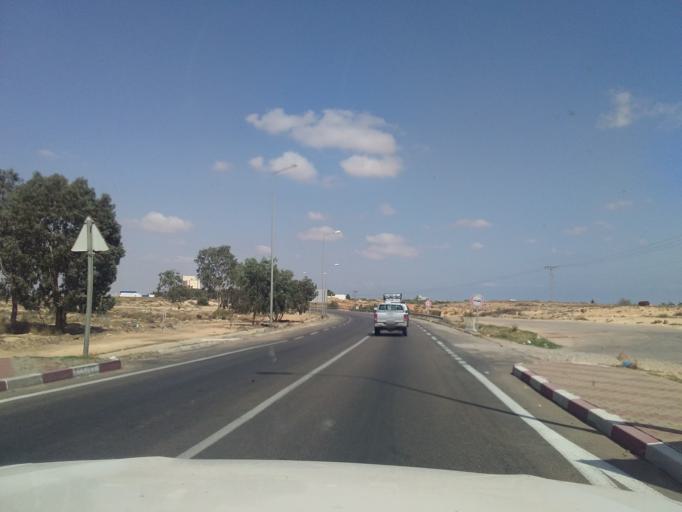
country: TN
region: Madanin
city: Medenine
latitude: 33.5919
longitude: 10.3138
